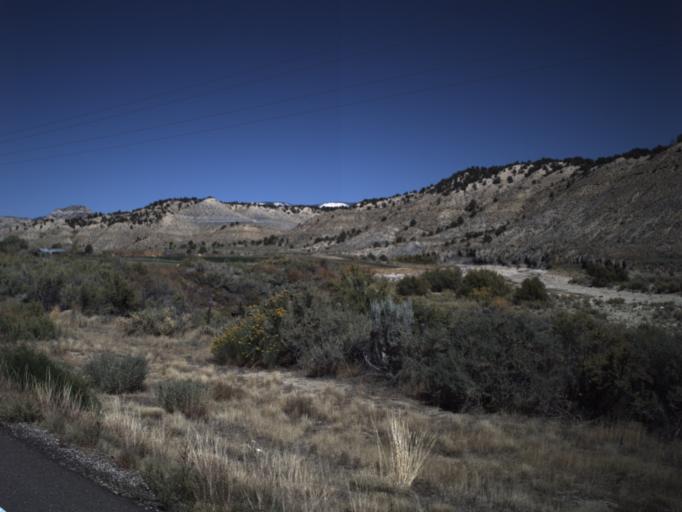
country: US
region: Utah
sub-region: Garfield County
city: Panguitch
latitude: 37.5957
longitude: -112.0619
